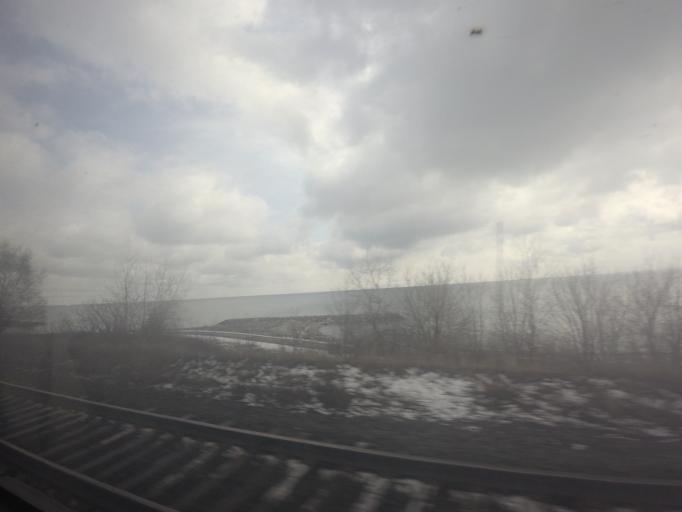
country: CA
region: Ontario
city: Scarborough
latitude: 43.7713
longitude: -79.1390
